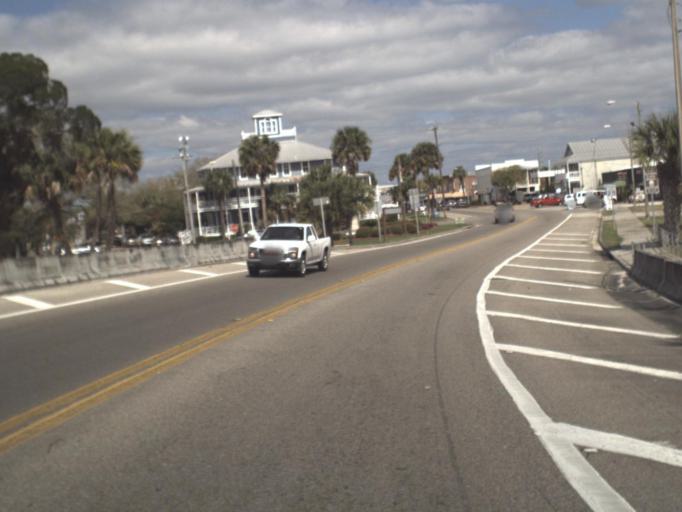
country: US
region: Florida
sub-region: Franklin County
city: Apalachicola
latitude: 29.7249
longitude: -84.9828
